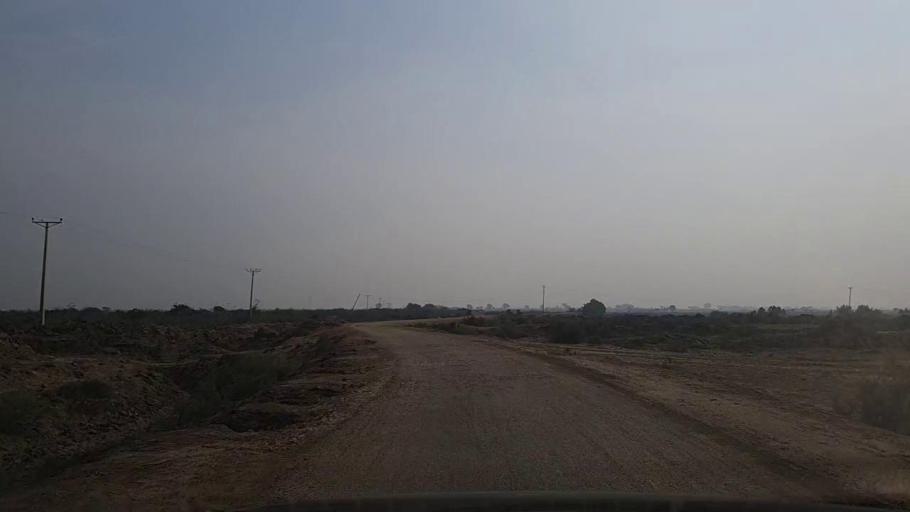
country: PK
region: Sindh
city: Mirpur Sakro
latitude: 24.3856
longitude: 67.7529
